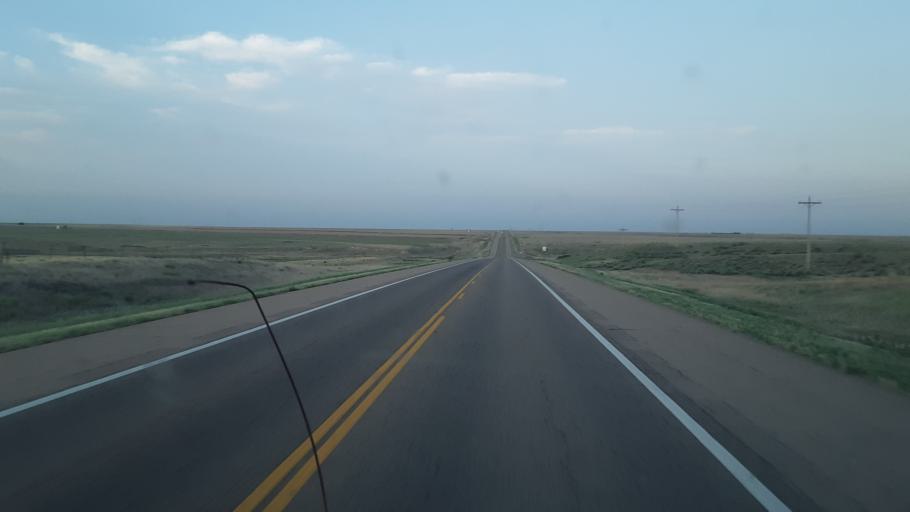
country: US
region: Kansas
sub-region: Kearny County
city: Lakin
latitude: 37.9440
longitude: -101.4492
